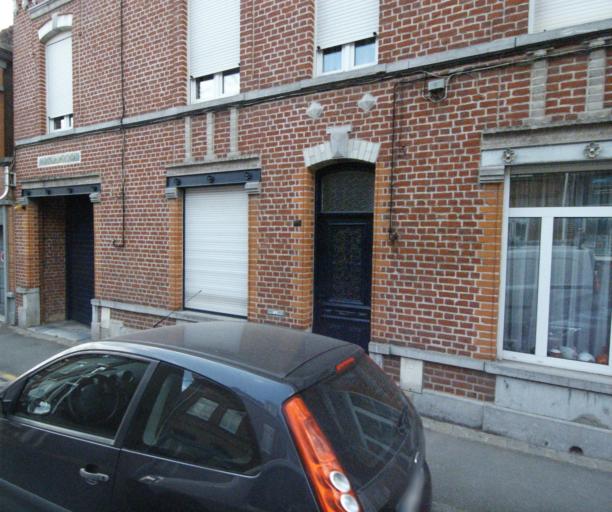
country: FR
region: Nord-Pas-de-Calais
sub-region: Departement du Nord
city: Mouvaux
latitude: 50.7002
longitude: 3.1336
